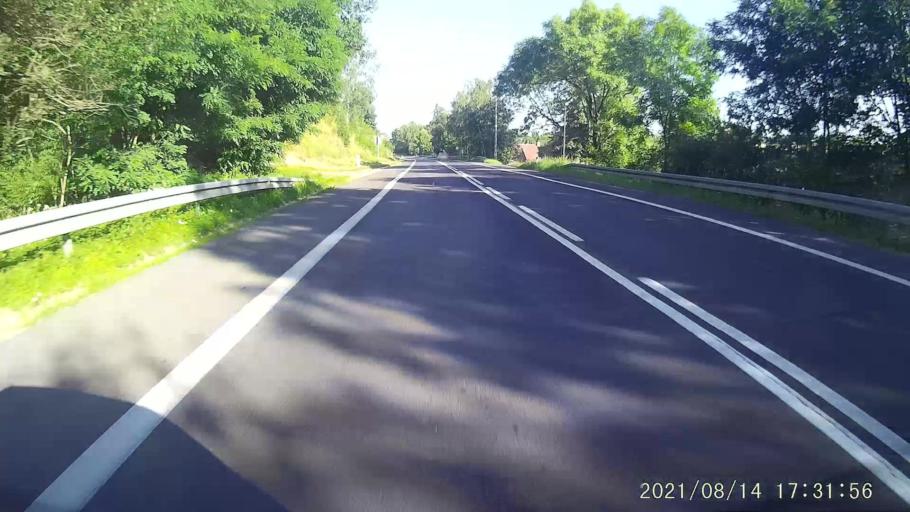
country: PL
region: Lower Silesian Voivodeship
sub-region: Powiat jeleniogorski
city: Stara Kamienica
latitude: 50.9143
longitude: 15.6274
